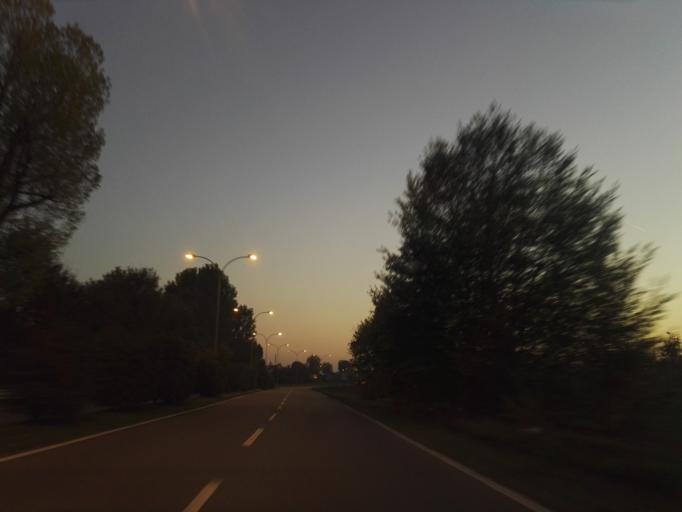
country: IT
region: Lombardy
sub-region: Citta metropolitana di Milano
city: San Bovio-San Felice
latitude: 45.4722
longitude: 9.3039
